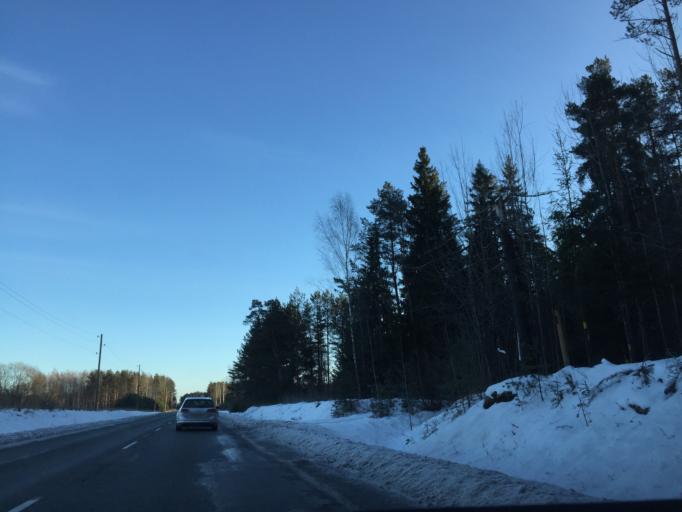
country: LV
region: Ogre
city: Jumprava
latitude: 56.6361
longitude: 24.8981
